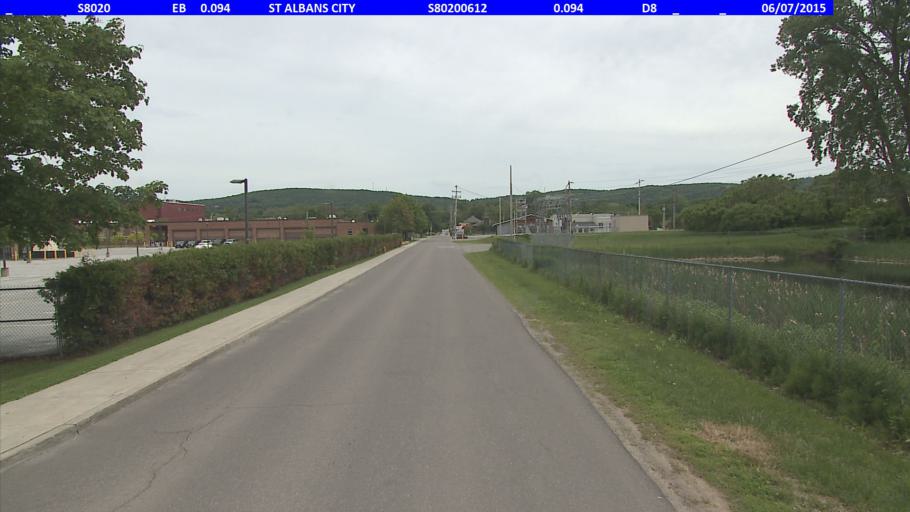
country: US
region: Vermont
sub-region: Franklin County
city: Saint Albans
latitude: 44.8085
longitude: -73.0919
